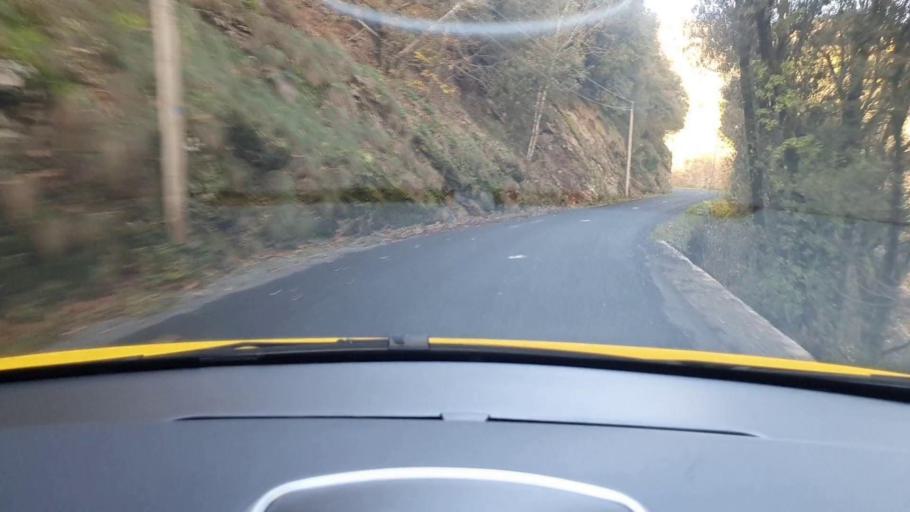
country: FR
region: Languedoc-Roussillon
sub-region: Departement du Gard
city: Valleraugue
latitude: 44.1063
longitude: 3.7286
